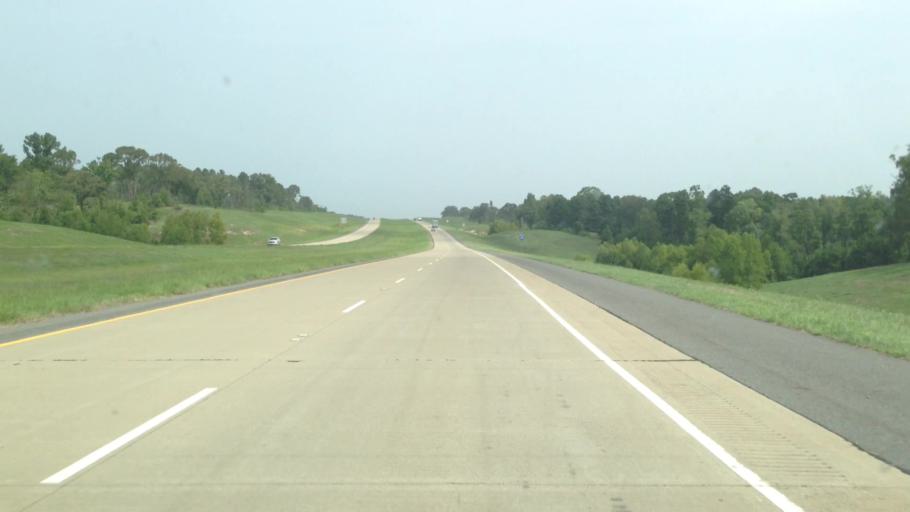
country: US
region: Louisiana
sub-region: Caddo Parish
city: Vivian
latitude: 32.9499
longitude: -93.8990
